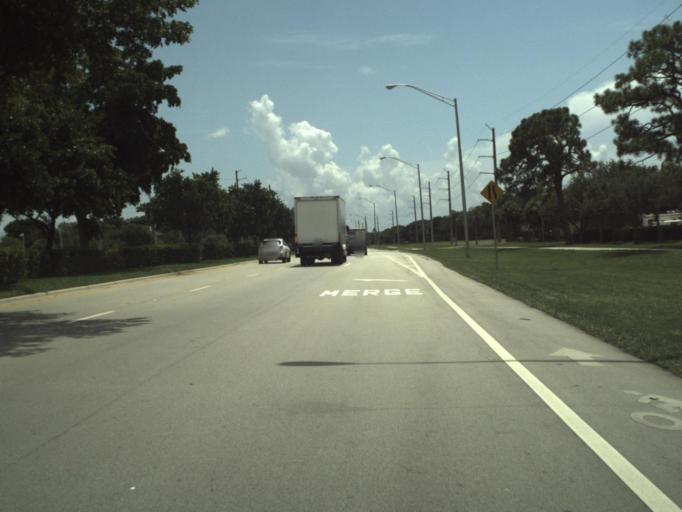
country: US
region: Florida
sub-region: Palm Beach County
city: Boca Pointe
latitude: 26.3042
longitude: -80.1491
